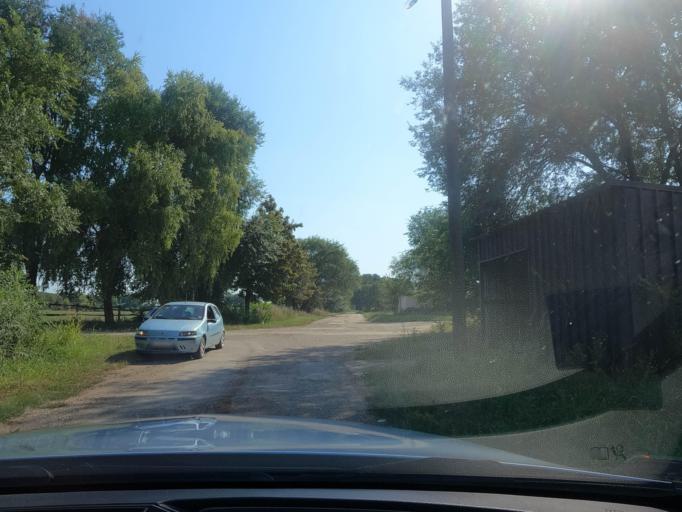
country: RS
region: Autonomna Pokrajina Vojvodina
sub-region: Juznobacki Okrug
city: Becej
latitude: 45.6555
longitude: 19.9000
